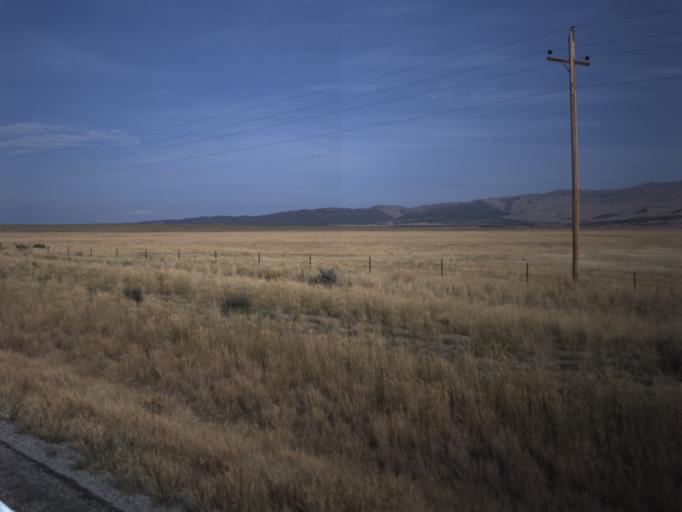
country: US
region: Idaho
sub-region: Oneida County
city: Malad City
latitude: 41.9655
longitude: -113.0317
